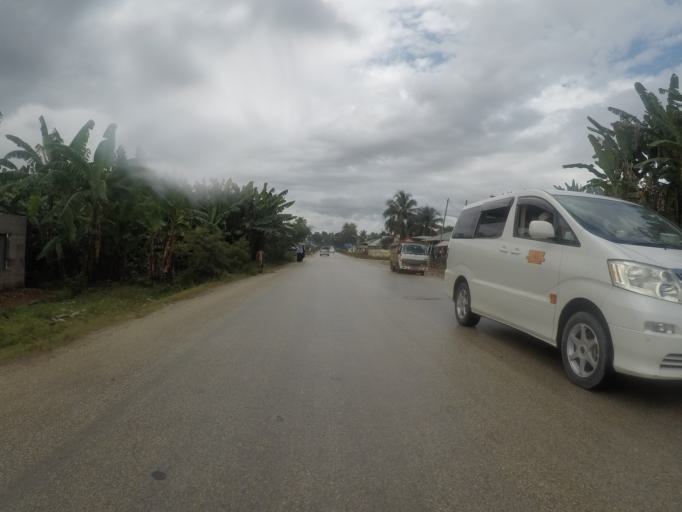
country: TZ
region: Zanzibar Central/South
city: Koani
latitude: -6.0417
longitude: 39.2292
